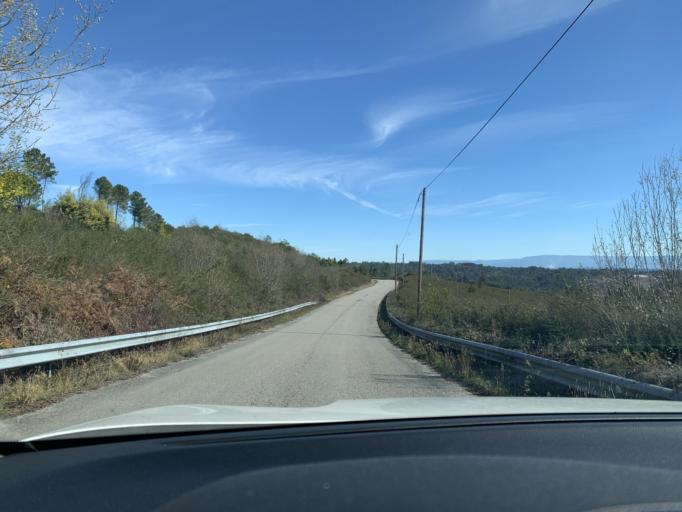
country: PT
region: Viseu
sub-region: Concelho de Tondela
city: Tondela
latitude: 40.6050
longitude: -8.0391
